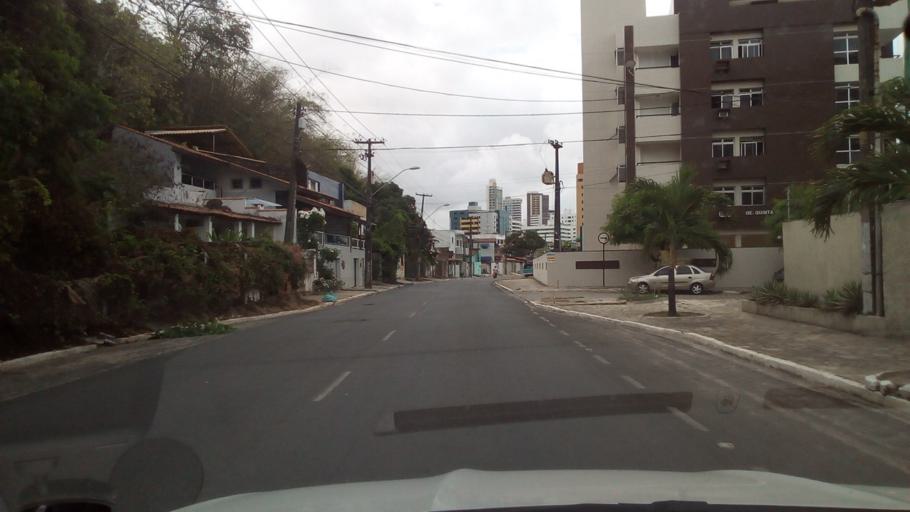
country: BR
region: Paraiba
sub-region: Joao Pessoa
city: Joao Pessoa
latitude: -7.1295
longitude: -34.8251
